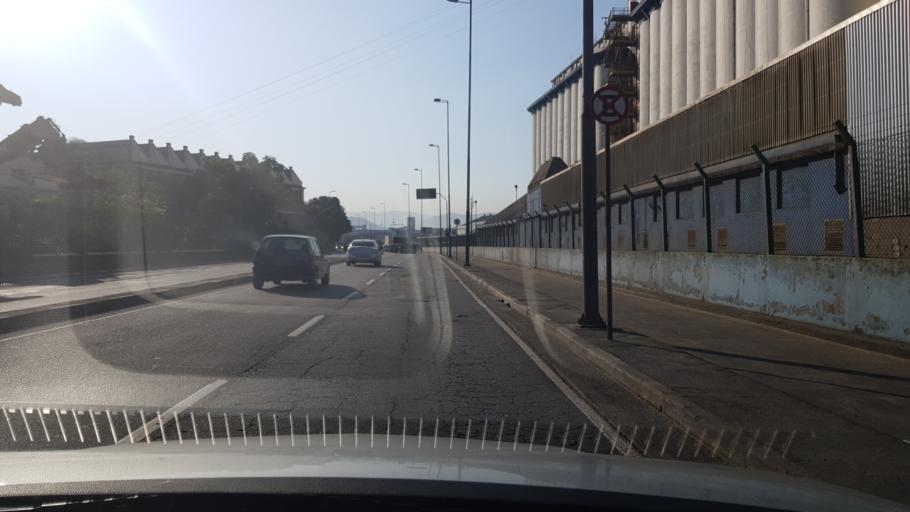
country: BR
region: Sao Paulo
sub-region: Santos
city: Santos
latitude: -23.9555
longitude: -46.3097
